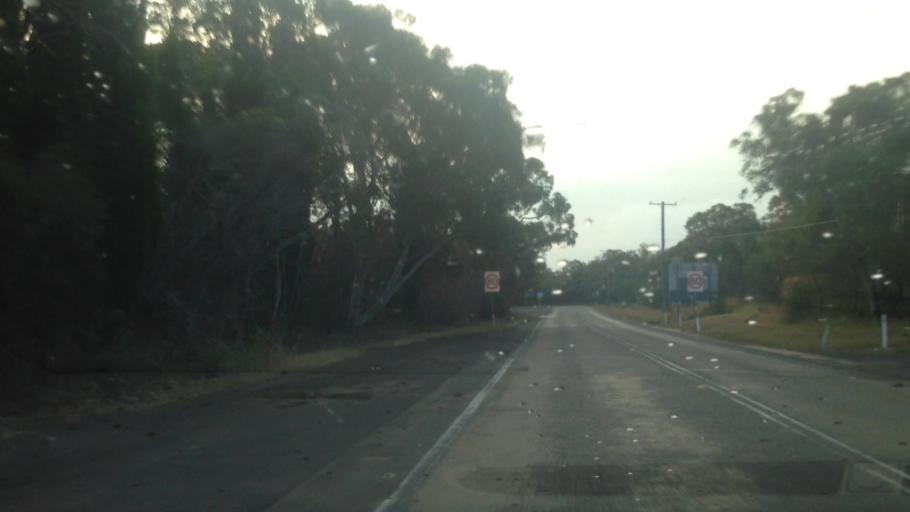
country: AU
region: New South Wales
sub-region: Wyong Shire
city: Buff Point
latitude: -33.1982
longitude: 151.5219
